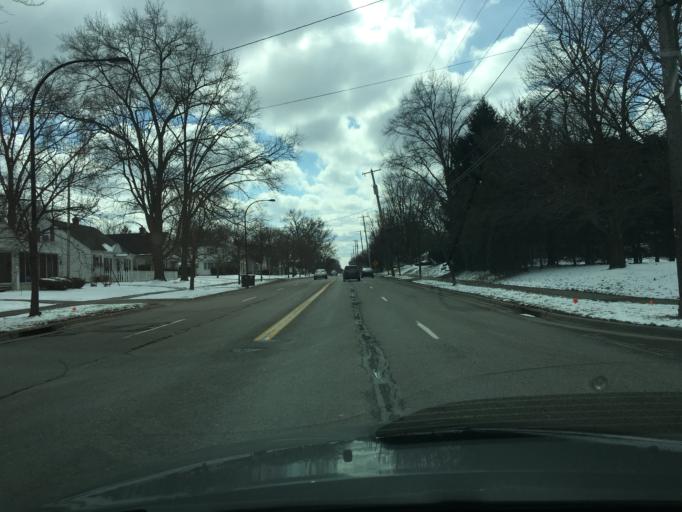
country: US
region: Ohio
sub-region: Summit County
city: Fairlawn
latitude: 41.1050
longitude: -81.5693
